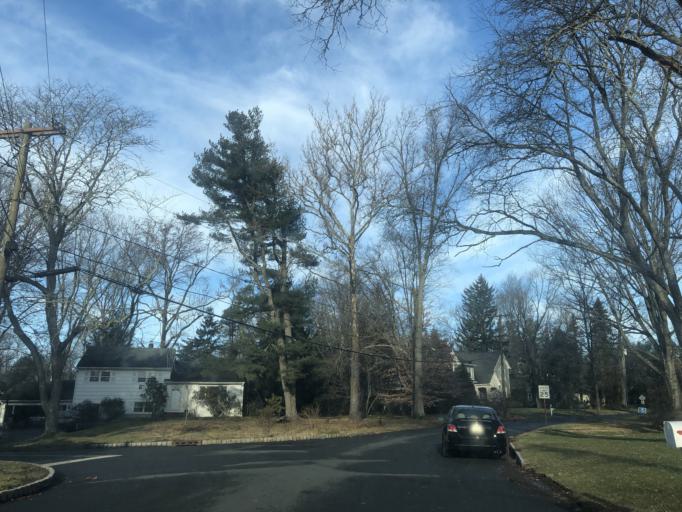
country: US
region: New Jersey
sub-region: Somerset County
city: Kingston
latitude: 40.3670
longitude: -74.6273
